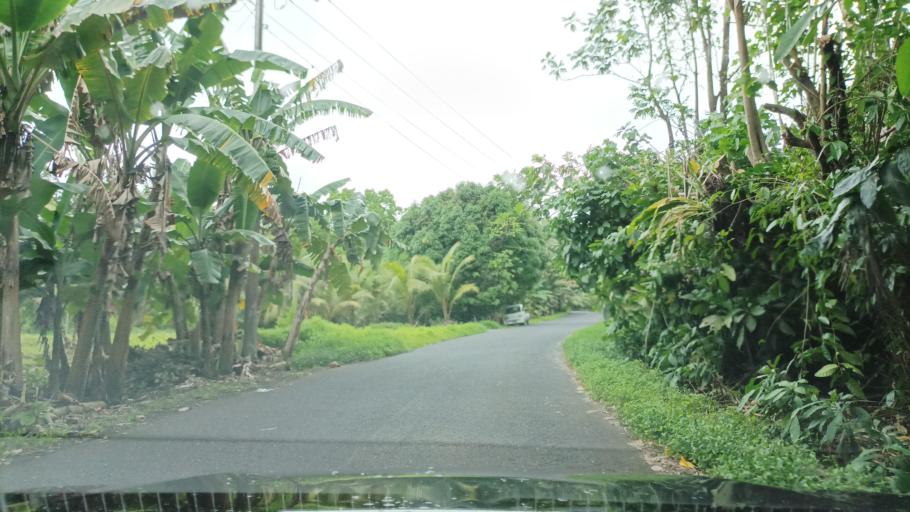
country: FM
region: Pohnpei
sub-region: Kolonia Municipality
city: Kolonia
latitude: 6.9595
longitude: 158.2783
